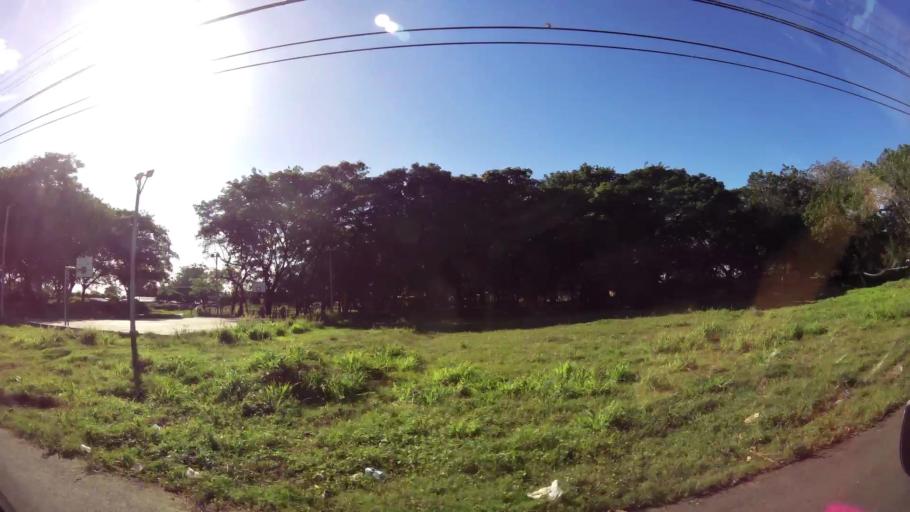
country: CR
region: Guanacaste
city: Belen
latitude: 10.4430
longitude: -85.5538
